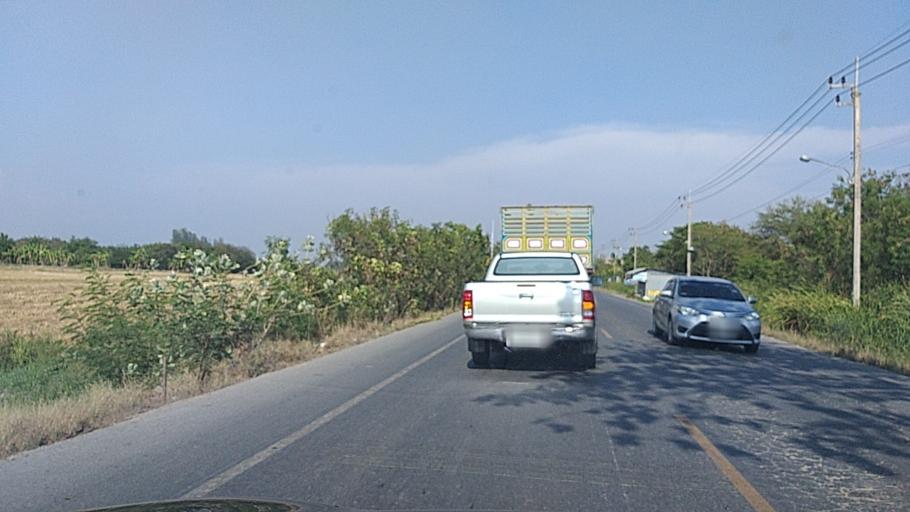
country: TH
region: Nonthaburi
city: Bang Yai
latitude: 13.8800
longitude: 100.3088
